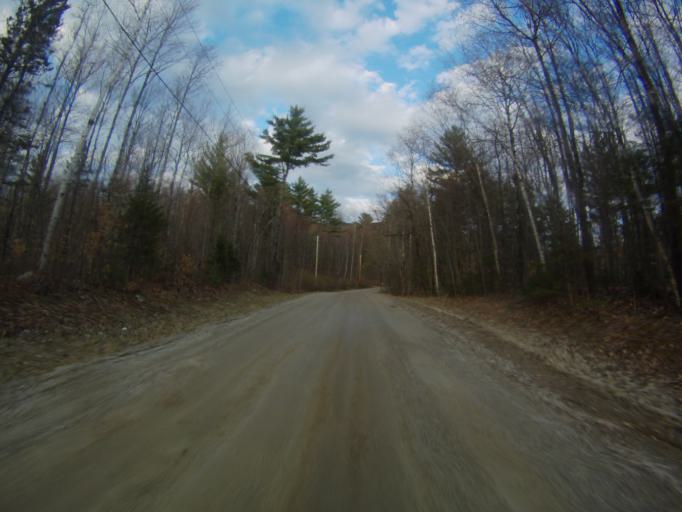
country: US
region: Vermont
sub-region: Rutland County
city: Brandon
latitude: 43.8553
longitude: -73.0018
